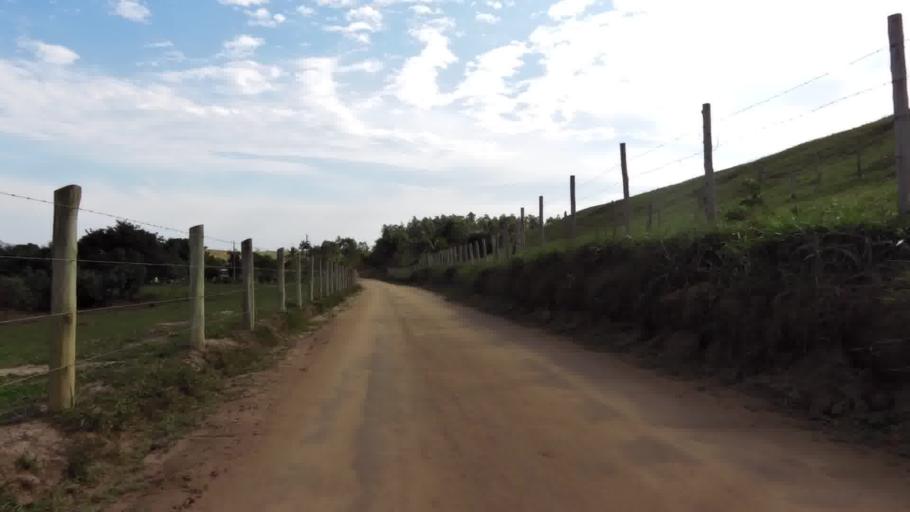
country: BR
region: Espirito Santo
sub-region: Piuma
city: Piuma
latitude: -20.8191
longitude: -40.7399
